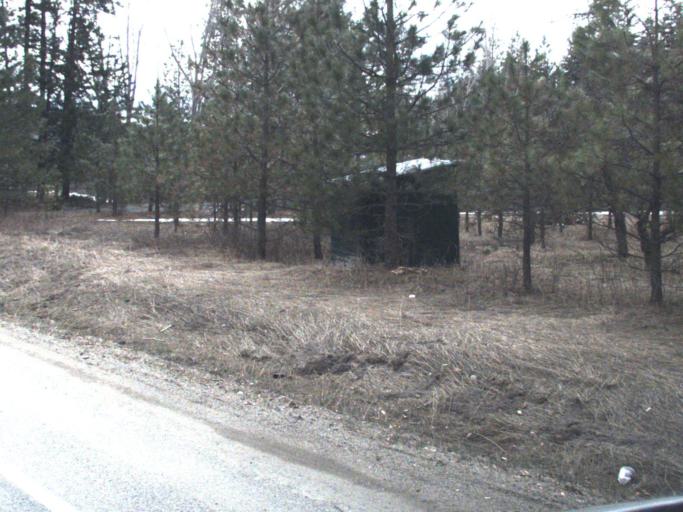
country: US
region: Washington
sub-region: Pend Oreille County
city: Newport
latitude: 48.2764
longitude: -117.2646
